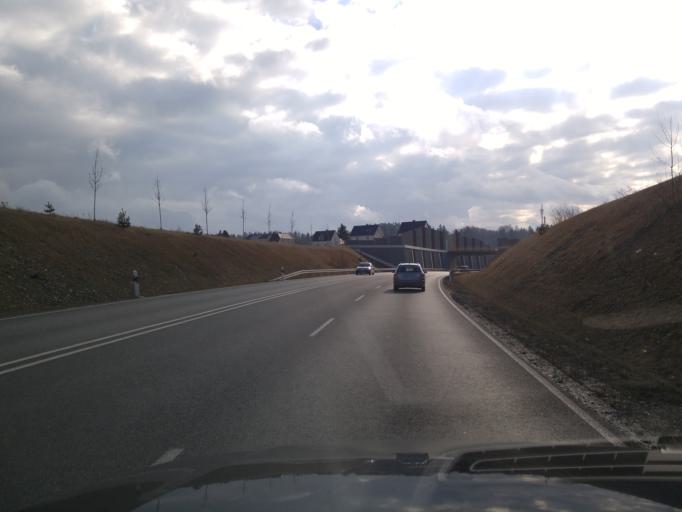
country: DE
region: Saxony
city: Hirschfeld
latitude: 50.6518
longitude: 12.4464
